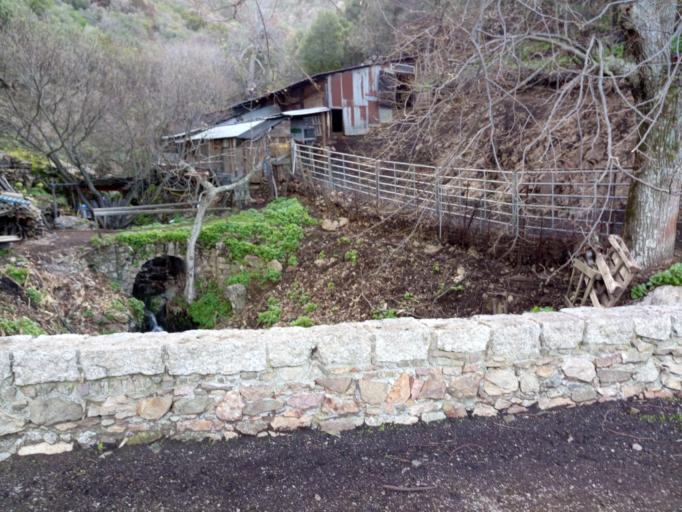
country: FR
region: Corsica
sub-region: Departement de la Corse-du-Sud
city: Cargese
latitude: 42.3439
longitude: 8.6625
